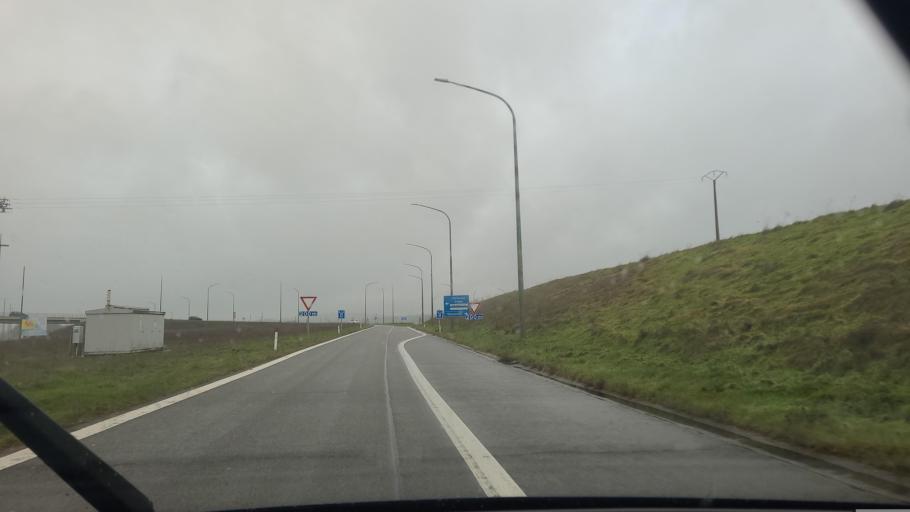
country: LU
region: Luxembourg
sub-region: Canton de Capellen
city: Steinfort
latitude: 49.6405
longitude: 5.8912
